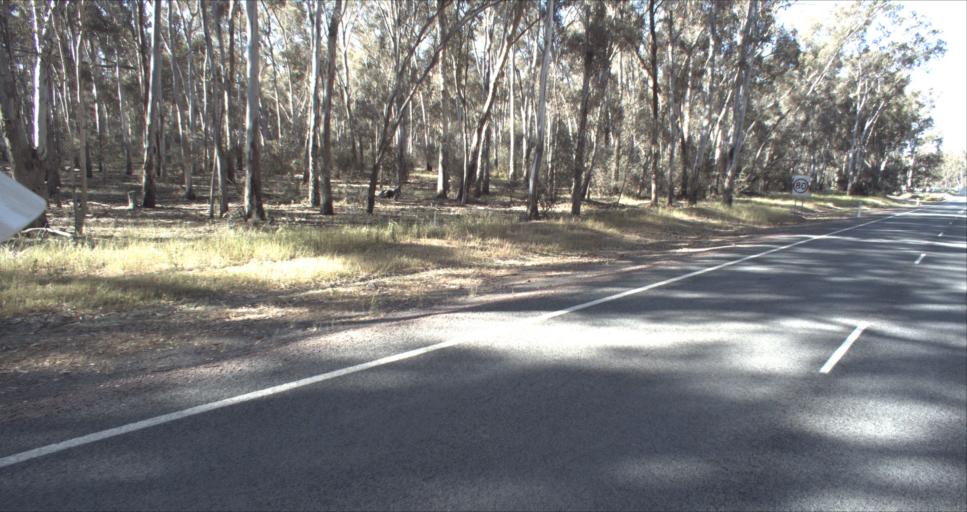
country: AU
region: New South Wales
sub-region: Leeton
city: Leeton
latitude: -34.6400
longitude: 146.3712
